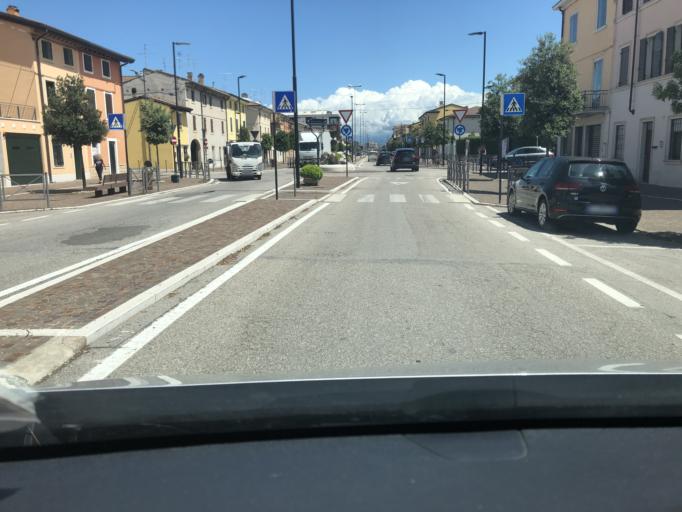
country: IT
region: Veneto
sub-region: Provincia di Verona
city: Villafranca di Verona
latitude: 45.3511
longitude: 10.8396
